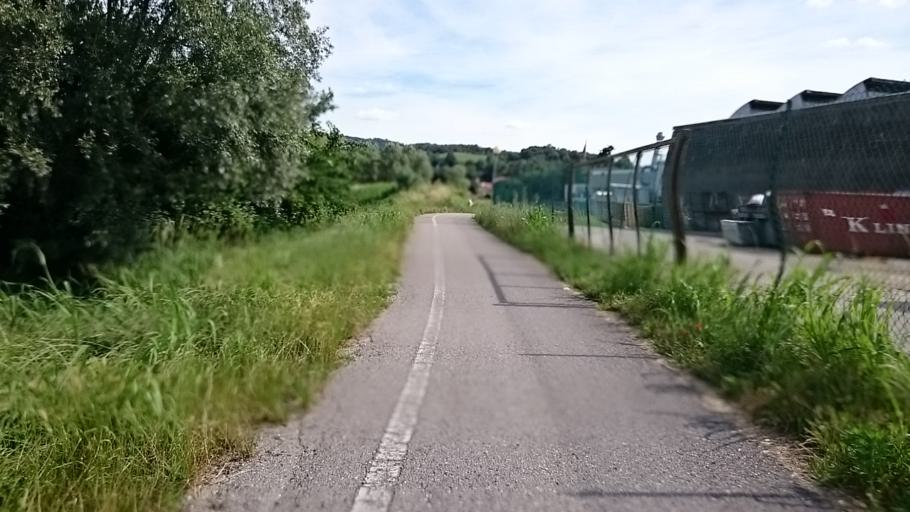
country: IT
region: Veneto
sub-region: Provincia di Vicenza
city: Arcugnano-Torri
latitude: 45.5085
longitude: 11.5702
